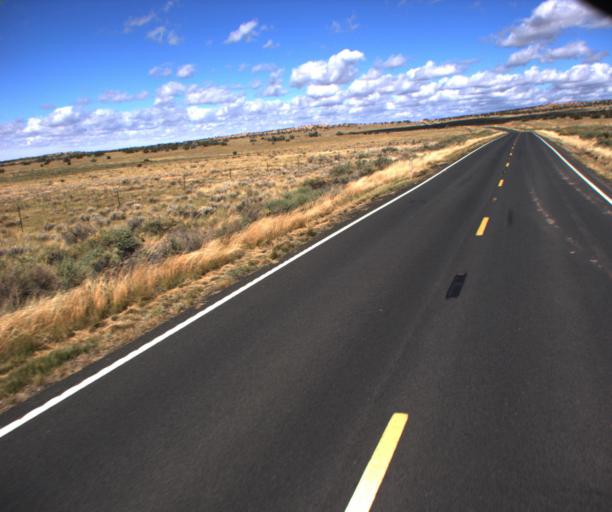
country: US
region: Arizona
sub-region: Apache County
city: Houck
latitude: 35.0550
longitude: -109.2764
